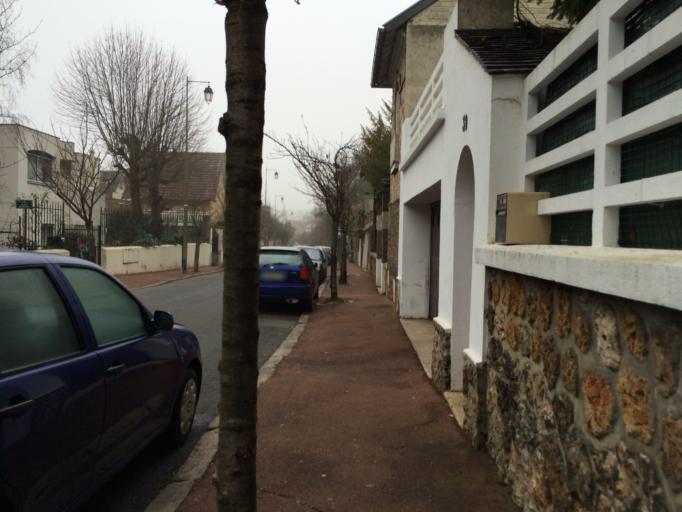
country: FR
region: Ile-de-France
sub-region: Departement des Hauts-de-Seine
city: Suresnes
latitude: 48.8577
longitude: 2.2172
